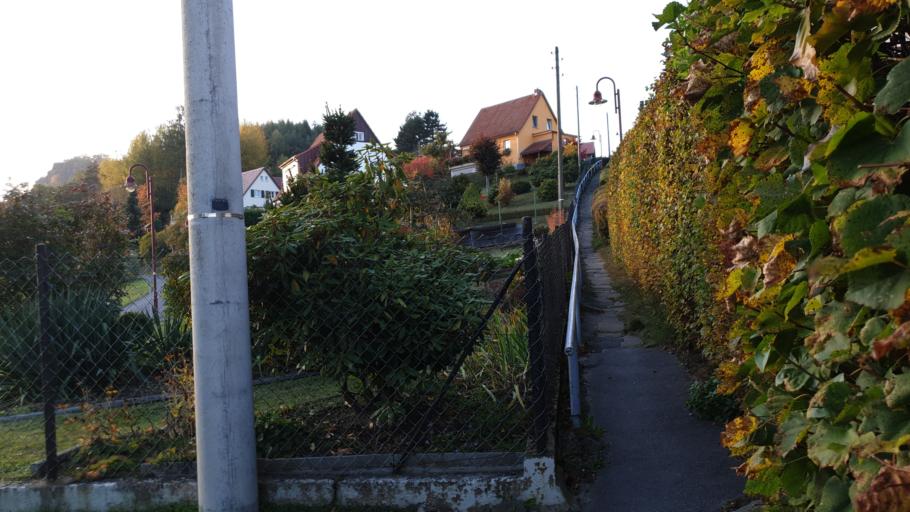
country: DE
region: Saxony
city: Bad Schandau
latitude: 50.9001
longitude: 14.1334
